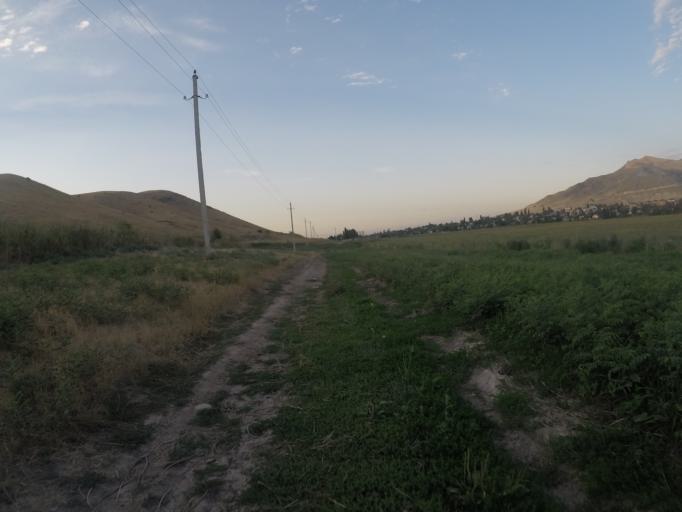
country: KG
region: Chuy
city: Bishkek
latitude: 42.7604
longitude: 74.6362
